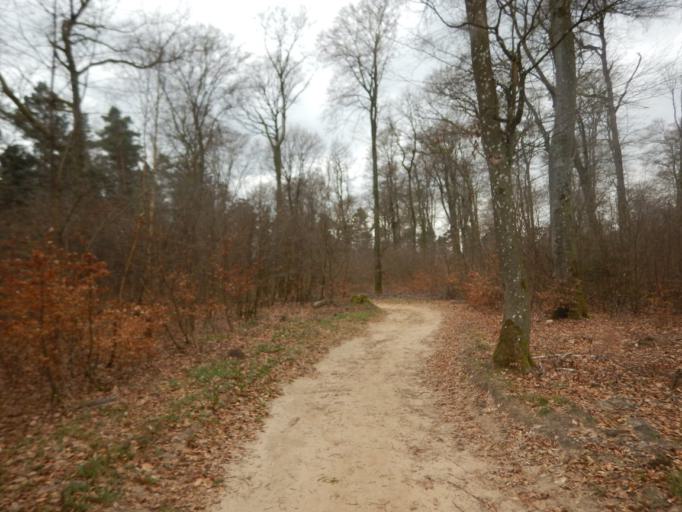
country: LU
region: Luxembourg
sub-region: Canton de Mersch
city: Lorentzweiler
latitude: 49.6949
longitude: 6.1544
